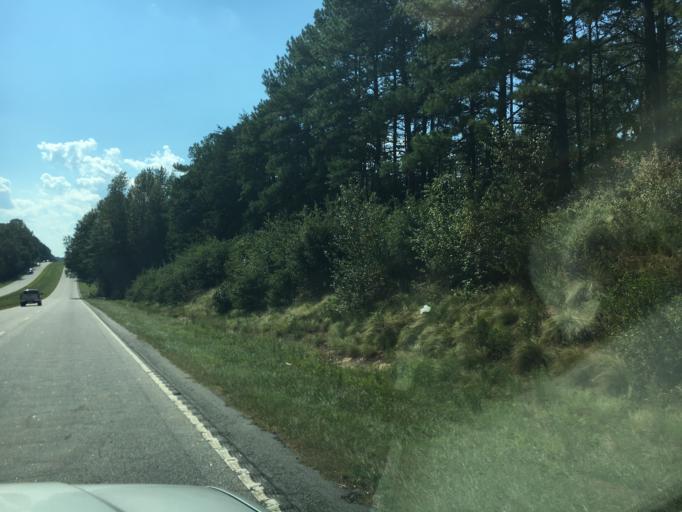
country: US
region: South Carolina
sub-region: Pickens County
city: Central
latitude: 34.7033
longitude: -82.7629
